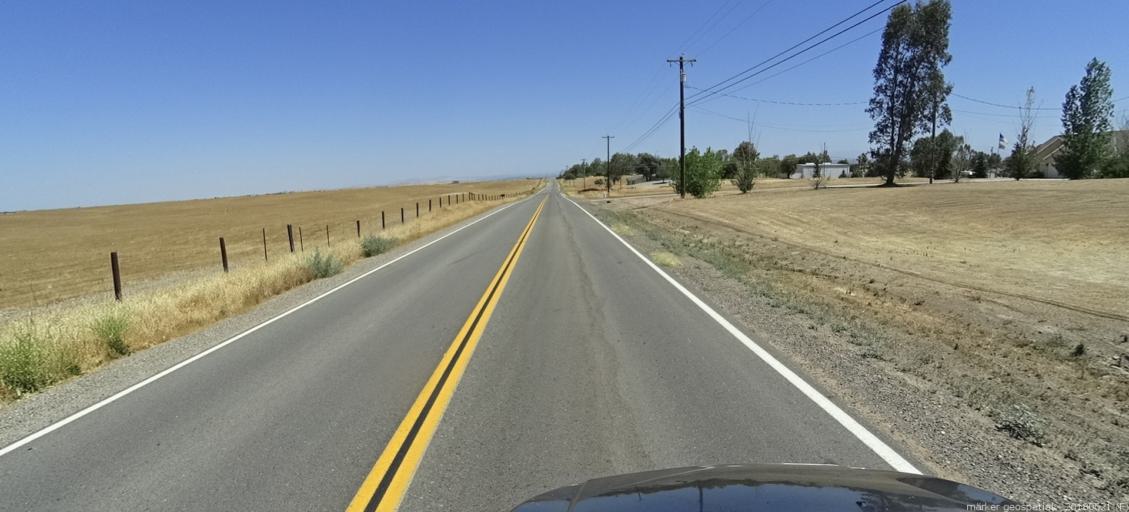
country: US
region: California
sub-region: Madera County
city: Bonadelle Ranchos-Madera Ranchos
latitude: 36.9868
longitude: -119.8937
